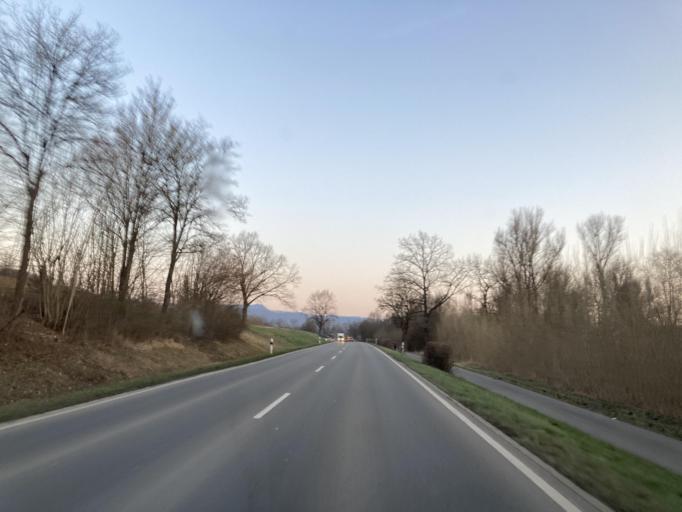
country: DE
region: Baden-Wuerttemberg
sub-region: Tuebingen Region
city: Dusslingen
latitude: 48.4649
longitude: 9.0725
